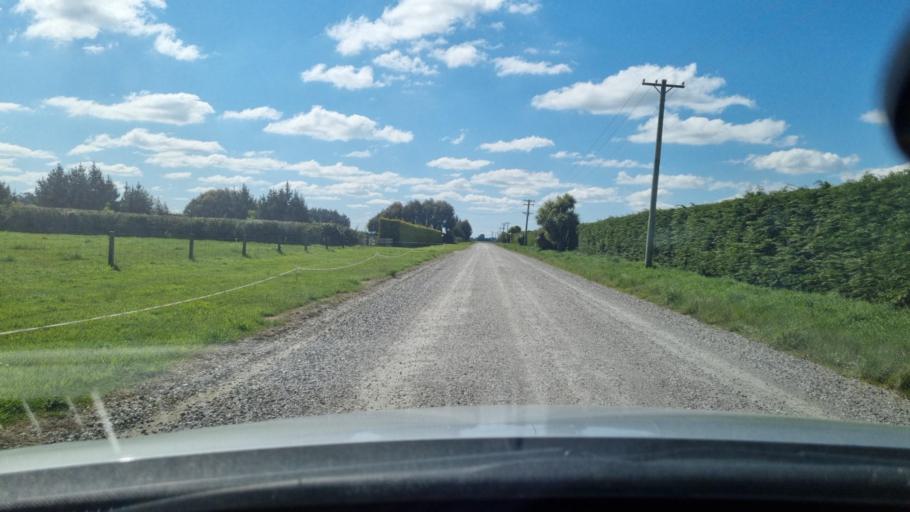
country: NZ
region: Southland
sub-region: Invercargill City
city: Invercargill
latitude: -46.3746
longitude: 168.2985
